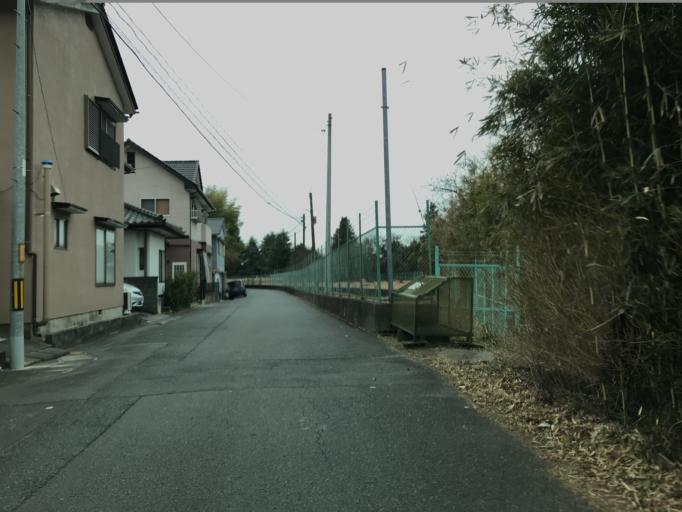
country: JP
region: Fukushima
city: Iwaki
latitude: 37.0630
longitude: 140.9068
